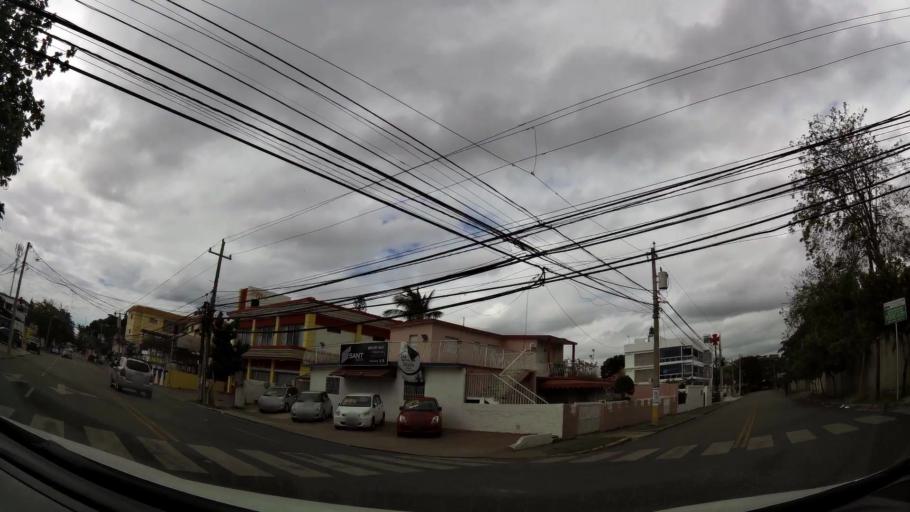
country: DO
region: Nacional
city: Bella Vista
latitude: 18.4754
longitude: -69.9581
